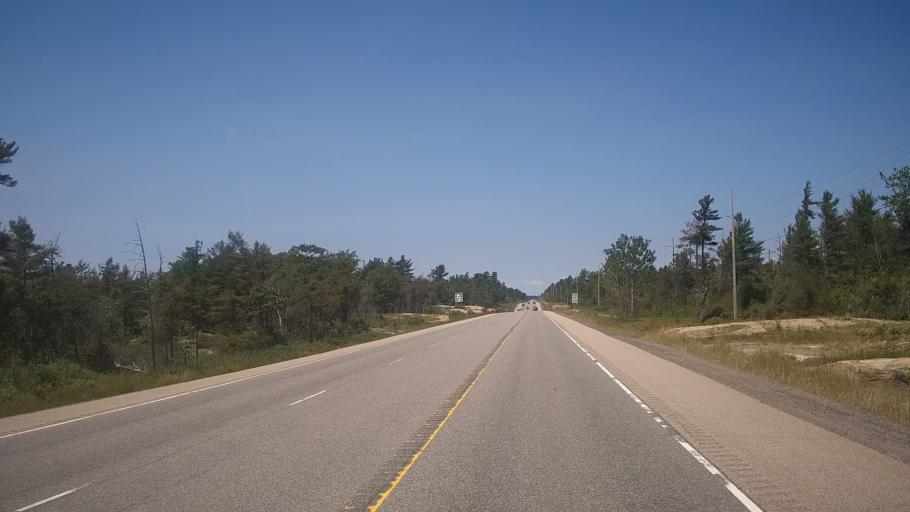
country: CA
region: Ontario
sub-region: Parry Sound District
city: Parry Sound
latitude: 45.6604
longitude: -80.4155
